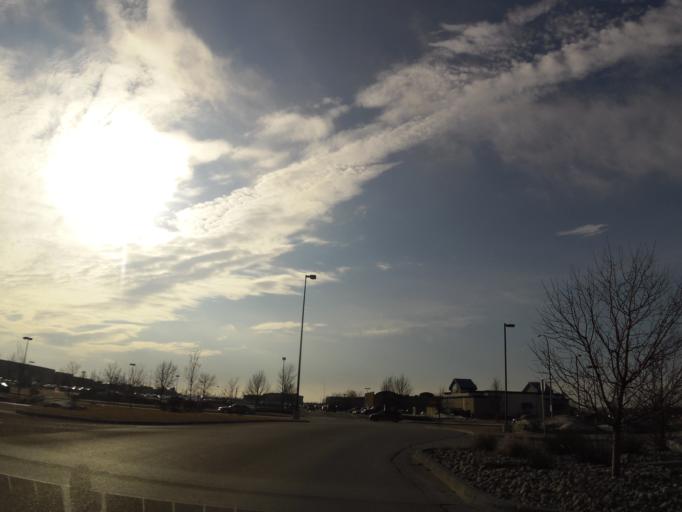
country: US
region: North Dakota
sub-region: Grand Forks County
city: Grand Forks
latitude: 47.8882
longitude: -97.0766
